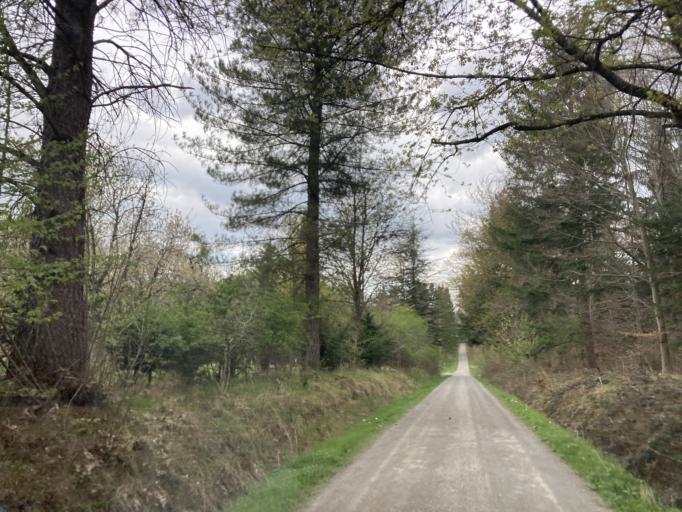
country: DE
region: Baden-Wuerttemberg
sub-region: Tuebingen Region
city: Kirchentellinsfurt
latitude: 48.5699
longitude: 9.1235
